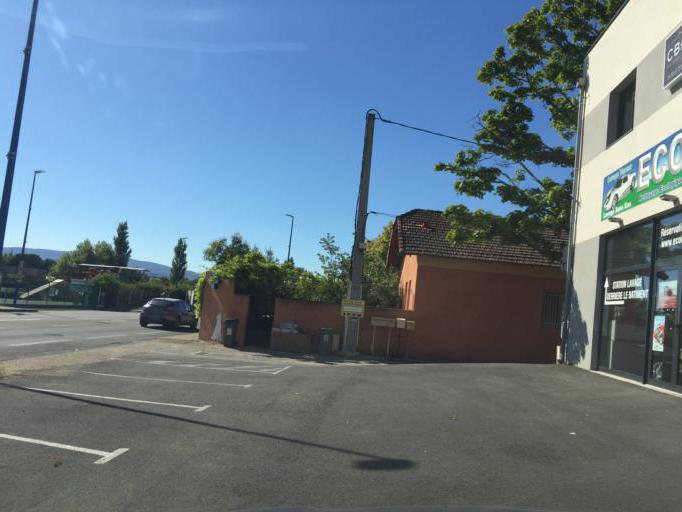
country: FR
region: Provence-Alpes-Cote d'Azur
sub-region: Departement du Vaucluse
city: Carpentras
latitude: 44.0388
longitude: 5.0497
